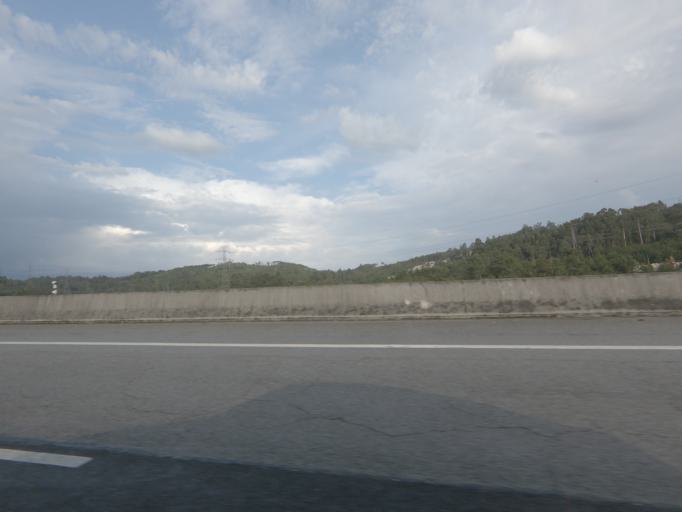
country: PT
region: Viseu
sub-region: Castro Daire
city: Castro Daire
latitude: 40.8244
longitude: -7.9354
